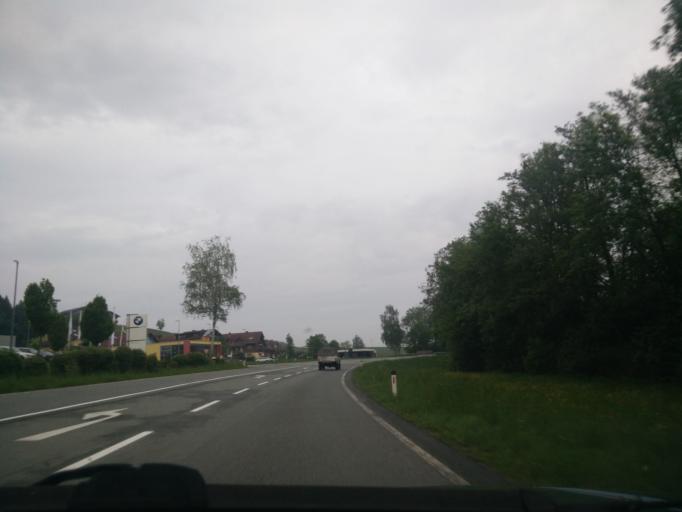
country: AT
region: Salzburg
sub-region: Politischer Bezirk Salzburg-Umgebung
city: Eugendorf
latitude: 47.8538
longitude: 13.1082
